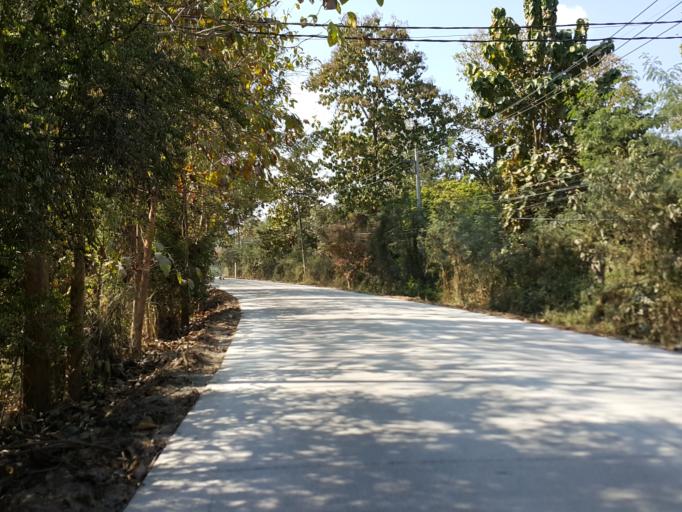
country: TH
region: Chiang Mai
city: Mae On
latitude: 18.8116
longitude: 99.2359
